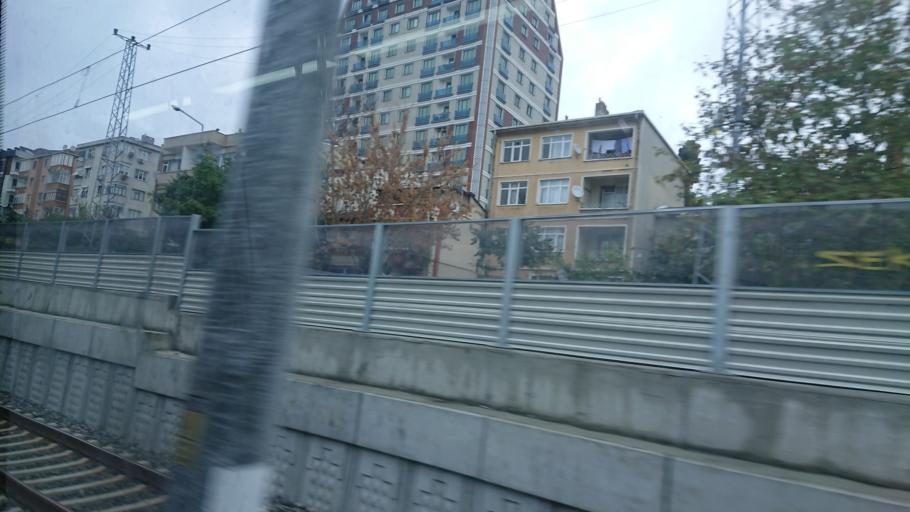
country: TR
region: Istanbul
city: Mahmutbey
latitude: 40.9918
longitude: 28.7715
